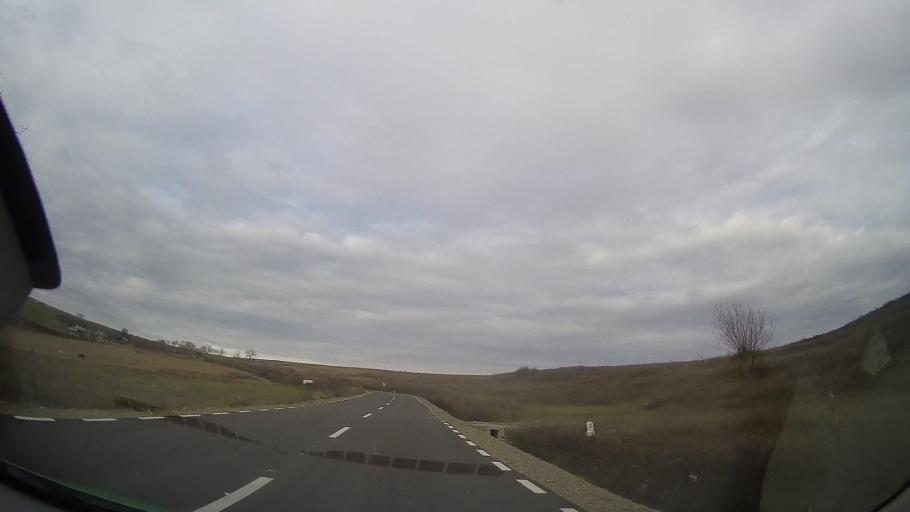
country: RO
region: Bistrita-Nasaud
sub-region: Comuna Teaca
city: Ocnita
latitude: 46.8247
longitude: 24.4794
